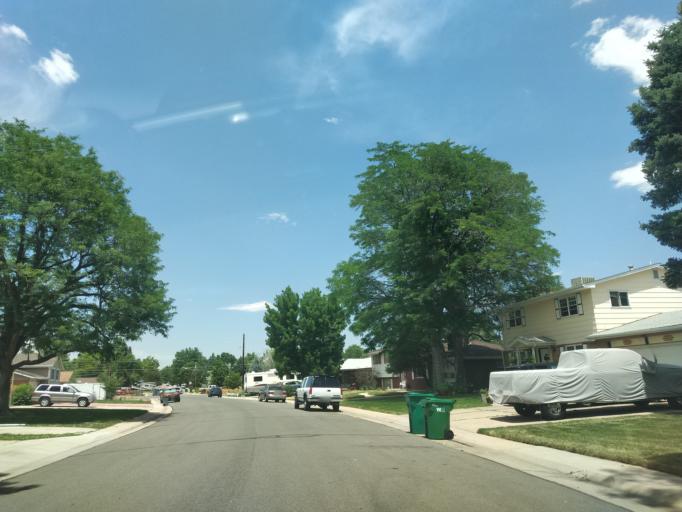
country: US
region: Colorado
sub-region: Jefferson County
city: Lakewood
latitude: 39.6811
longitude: -105.0920
